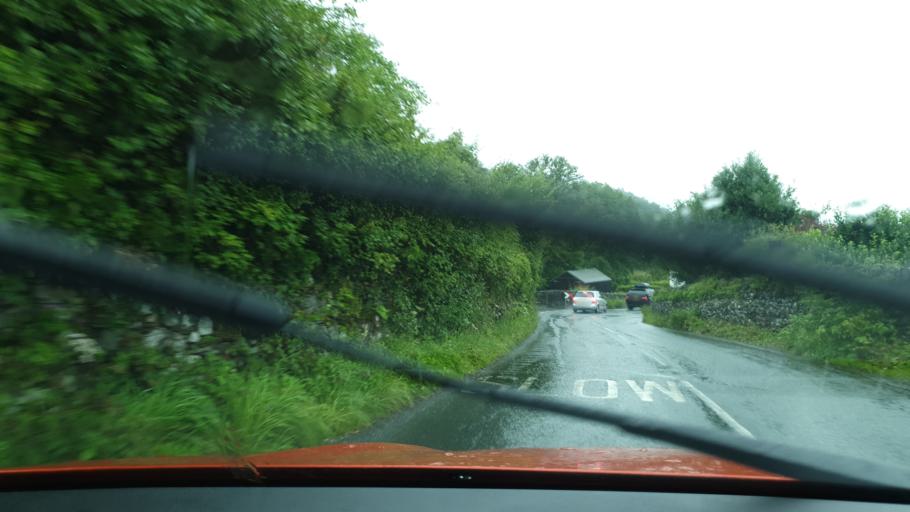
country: GB
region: England
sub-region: Cumbria
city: Ambleside
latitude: 54.3572
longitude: -3.0819
